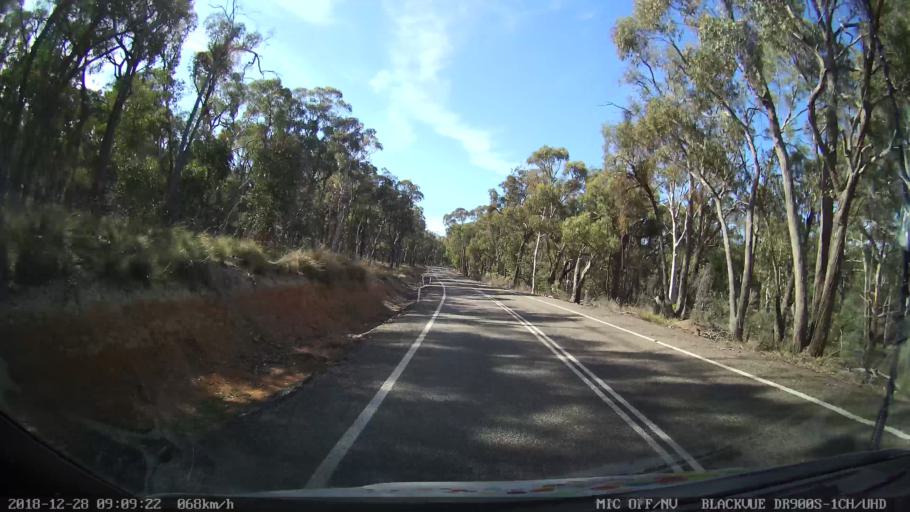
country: AU
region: New South Wales
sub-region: Upper Lachlan Shire
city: Crookwell
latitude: -34.2208
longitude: 149.3354
